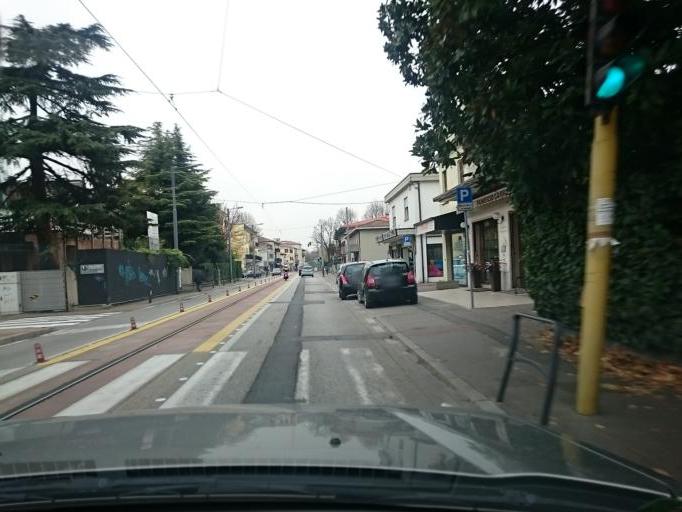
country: IT
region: Veneto
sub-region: Provincia di Padova
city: Mandriola-Sant'Agostino
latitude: 45.3826
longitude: 11.8689
